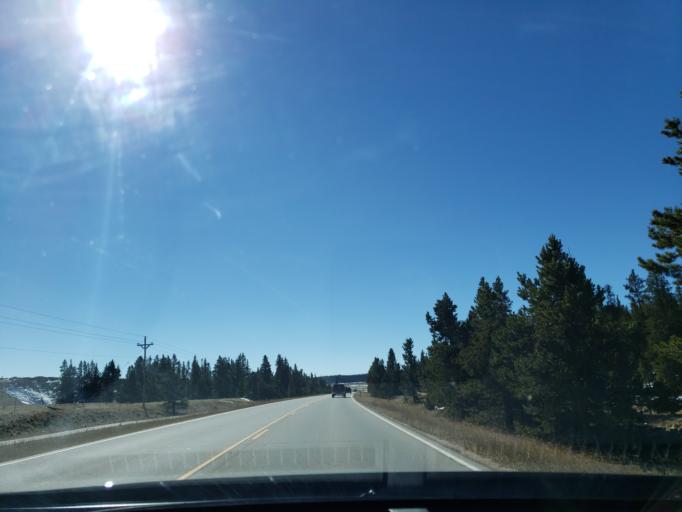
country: US
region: Colorado
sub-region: Park County
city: Fairplay
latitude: 39.2545
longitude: -106.0391
